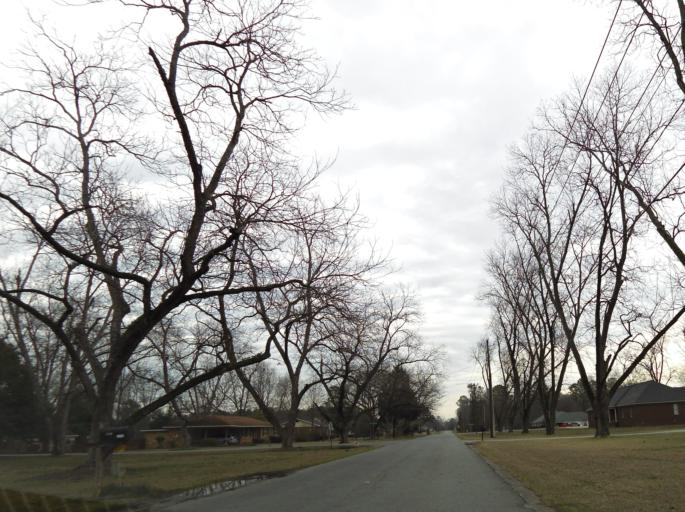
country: US
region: Georgia
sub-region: Houston County
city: Centerville
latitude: 32.7041
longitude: -83.6859
